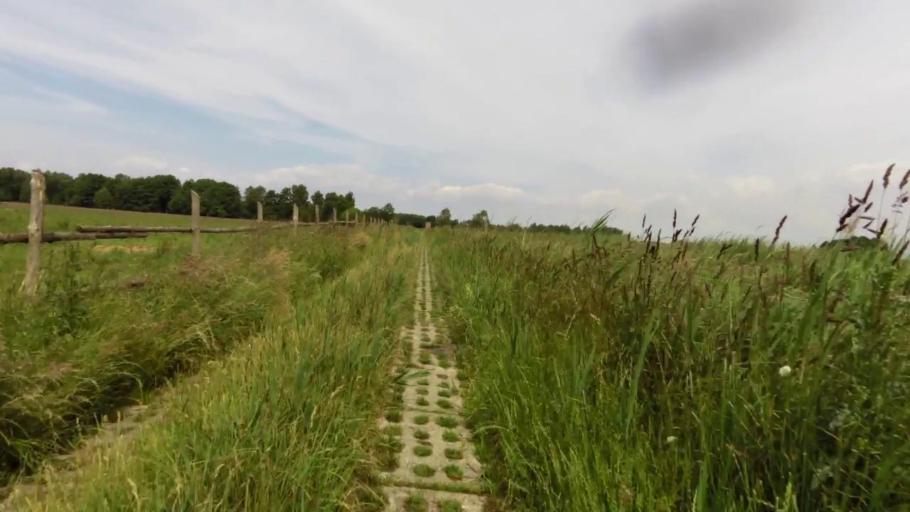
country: PL
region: West Pomeranian Voivodeship
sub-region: Powiat goleniowski
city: Stepnica
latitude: 53.7256
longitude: 14.6054
